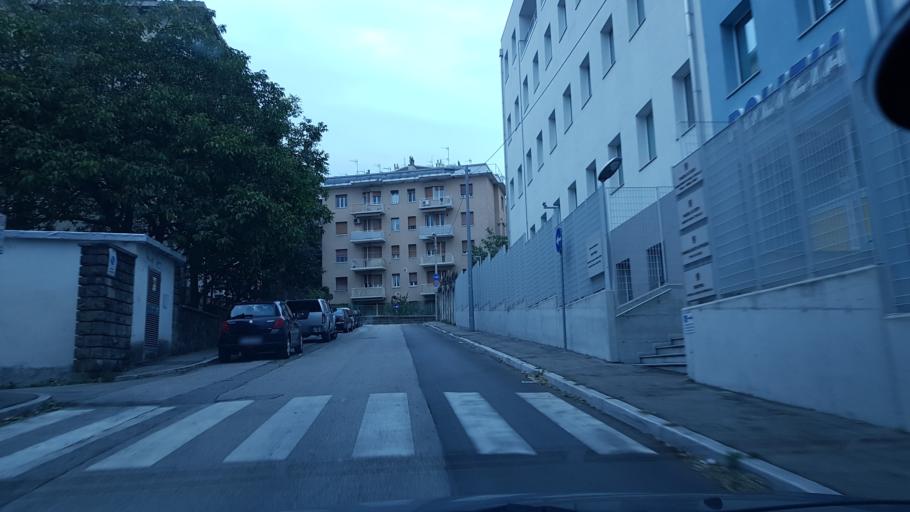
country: IT
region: Friuli Venezia Giulia
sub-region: Provincia di Trieste
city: Trieste
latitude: 45.6224
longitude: 13.8007
